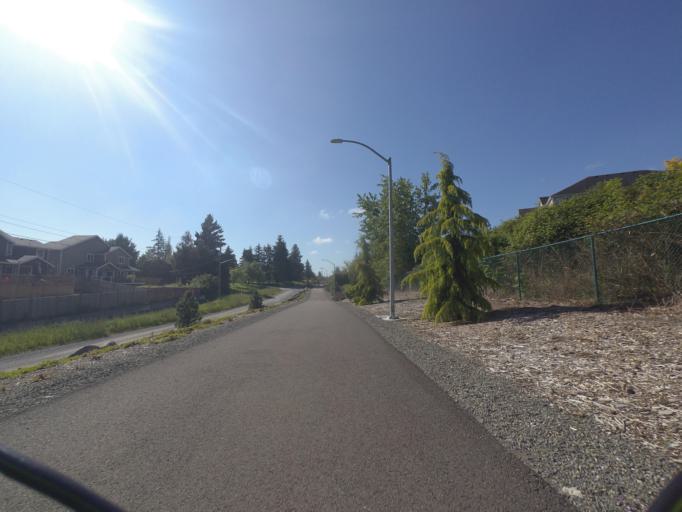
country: US
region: Washington
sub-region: Pierce County
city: Tacoma
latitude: 47.2194
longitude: -122.4157
